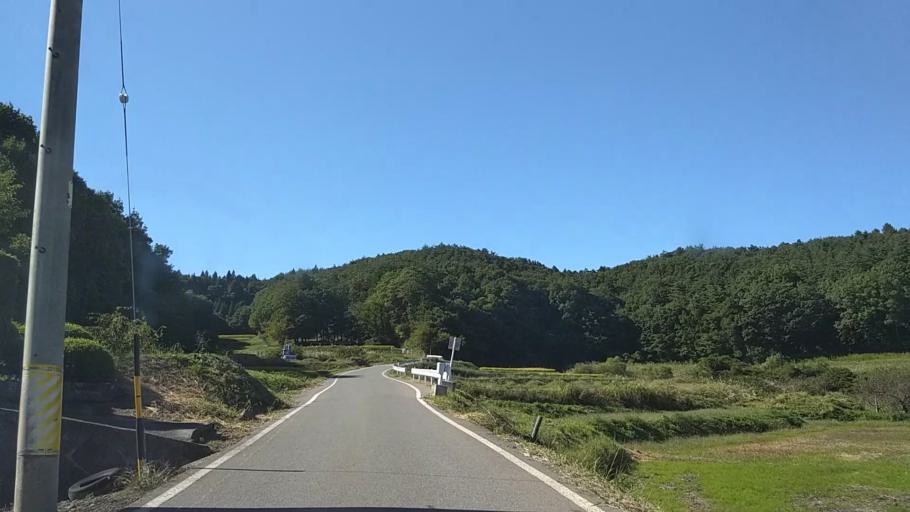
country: JP
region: Nagano
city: Nagano-shi
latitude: 36.5823
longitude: 138.1002
